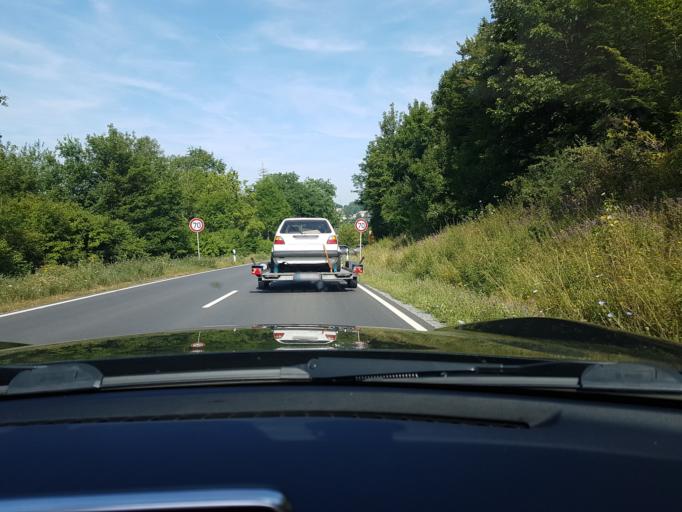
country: DE
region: Baden-Wuerttemberg
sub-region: Karlsruhe Region
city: Osterburken
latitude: 49.4262
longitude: 9.4295
